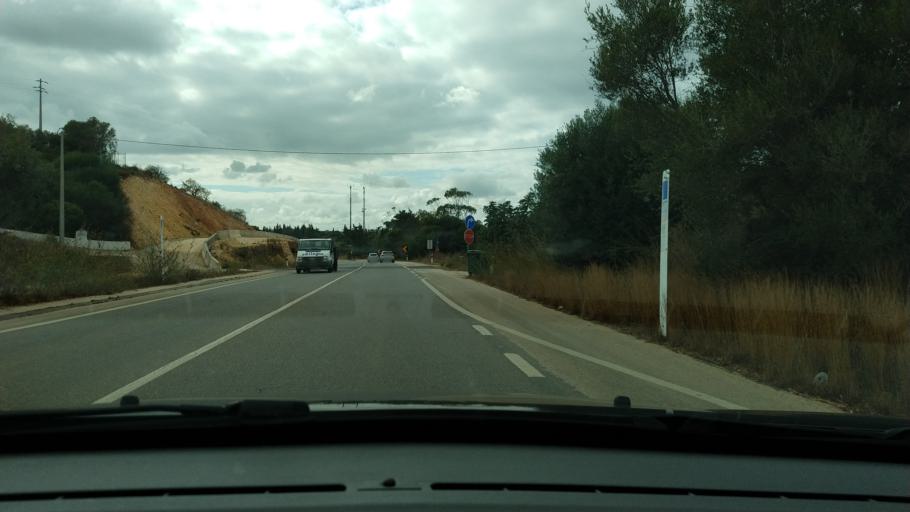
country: PT
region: Faro
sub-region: Lagos
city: Lagos
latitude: 37.0994
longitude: -8.7542
